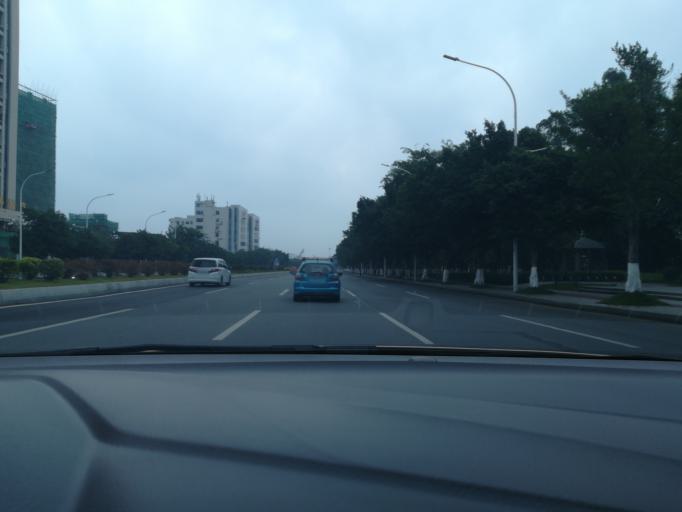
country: CN
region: Guangdong
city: Nansha
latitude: 22.8007
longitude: 113.5770
